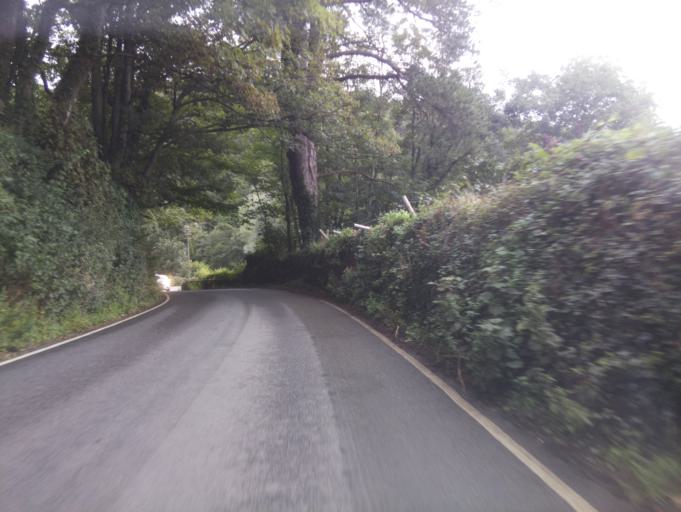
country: GB
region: England
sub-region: Devon
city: Dartmouth
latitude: 50.3192
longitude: -3.6137
